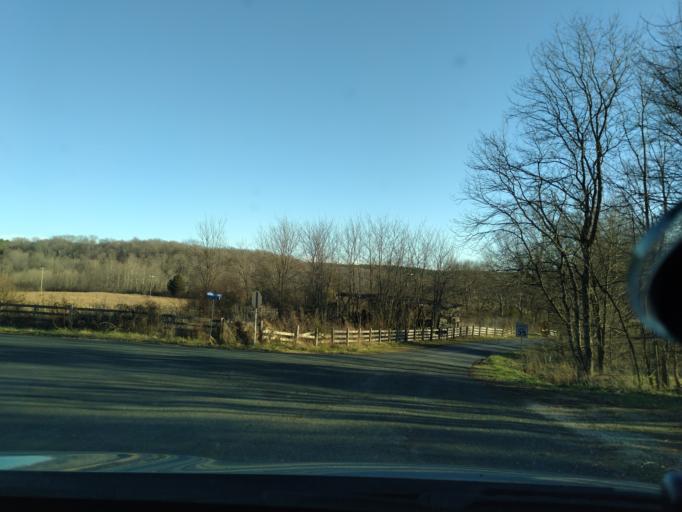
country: US
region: Virginia
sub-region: Appomattox County
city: Appomattox
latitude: 37.3751
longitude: -78.6399
